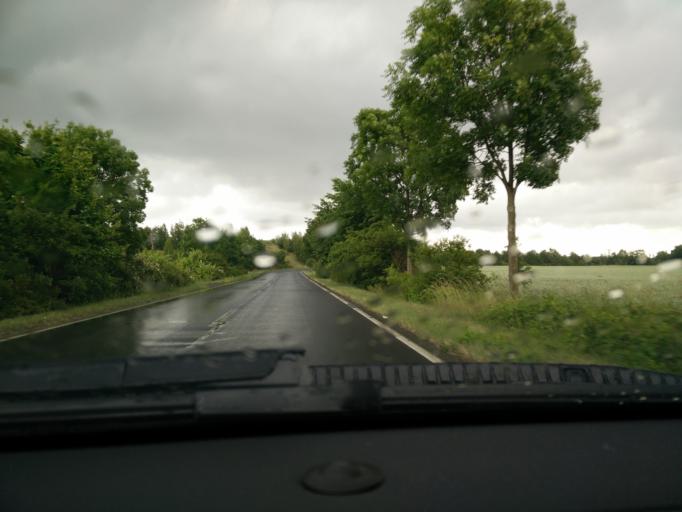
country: DE
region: Saxony
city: Trebsen
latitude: 51.2607
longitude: 12.7405
